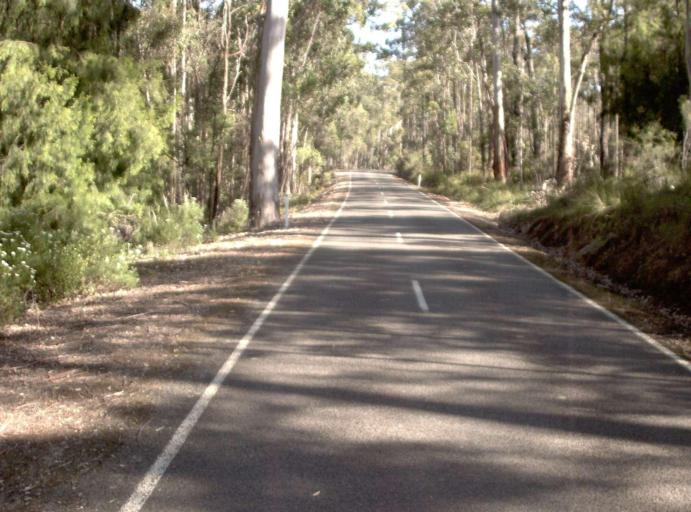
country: AU
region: Victoria
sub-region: East Gippsland
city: Lakes Entrance
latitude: -37.6182
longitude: 148.5123
